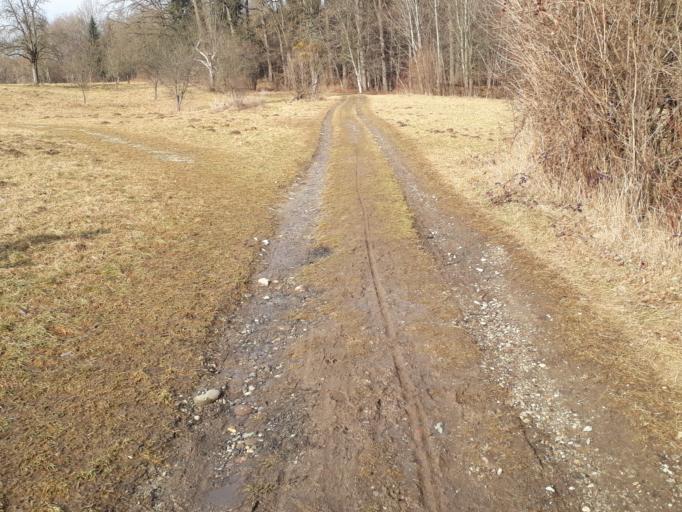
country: AT
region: Styria
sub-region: Politischer Bezirk Graz-Umgebung
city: Stattegg
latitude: 47.1167
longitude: 15.4197
